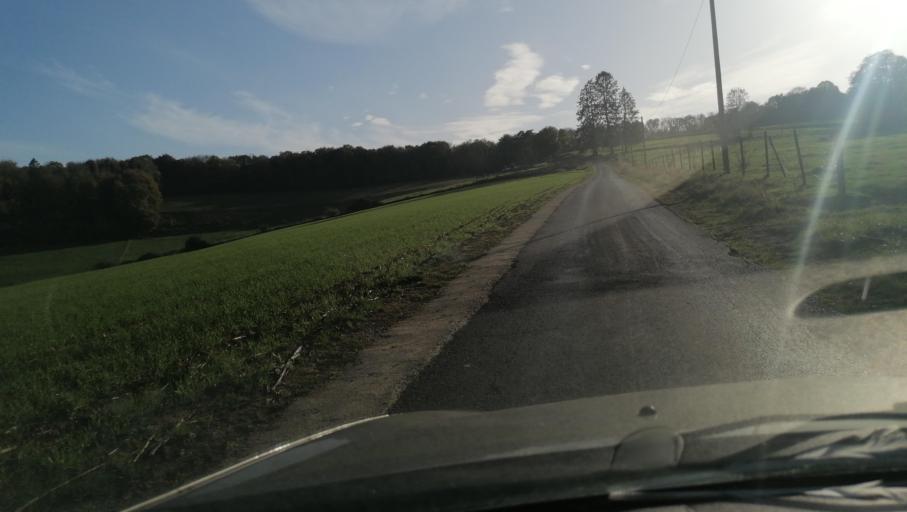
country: FR
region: Champagne-Ardenne
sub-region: Departement des Ardennes
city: La Francheville
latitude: 49.6894
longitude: 4.7283
